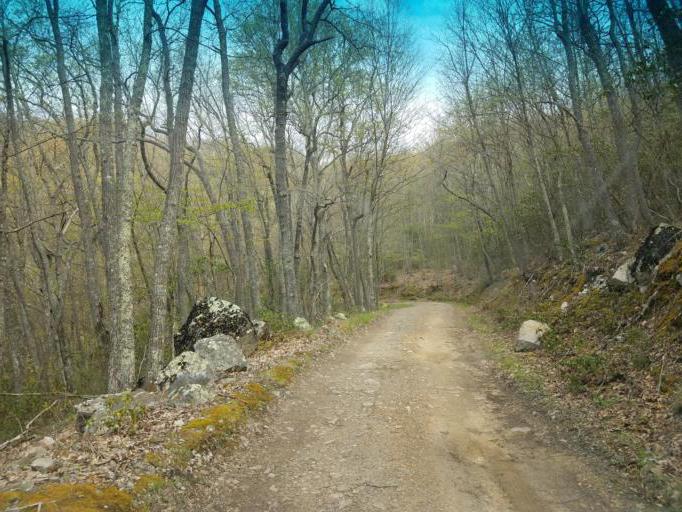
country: US
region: Virginia
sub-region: Smyth County
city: Marion
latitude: 36.7877
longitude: -81.4649
